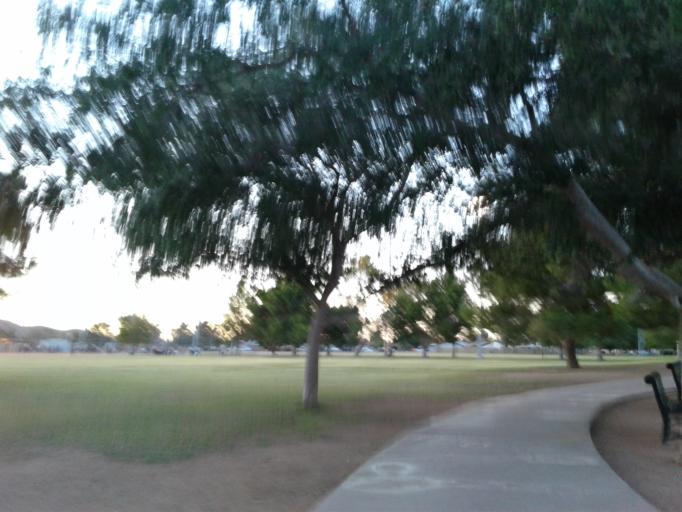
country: US
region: Arizona
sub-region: Maricopa County
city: Paradise Valley
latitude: 33.5986
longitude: -112.0064
